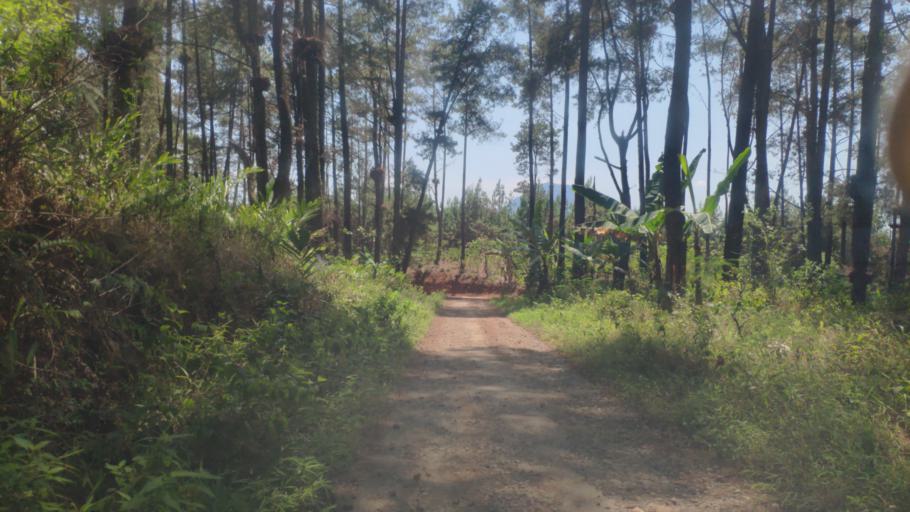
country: ID
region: Central Java
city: Buaran
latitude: -7.3003
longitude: 109.6300
